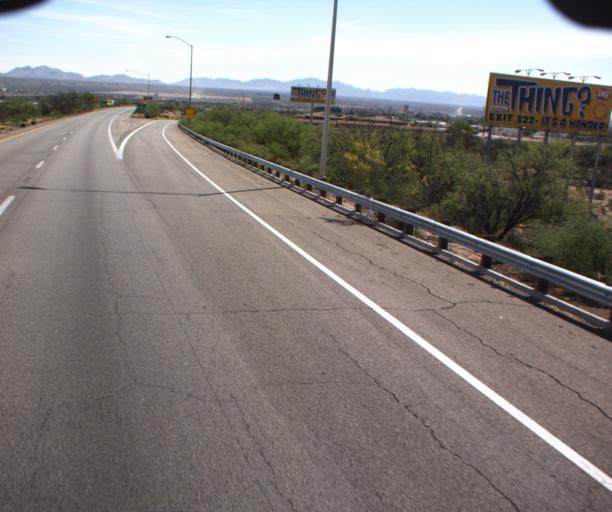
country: US
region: Arizona
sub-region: Cochise County
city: Benson
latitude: 31.9778
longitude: -110.3118
